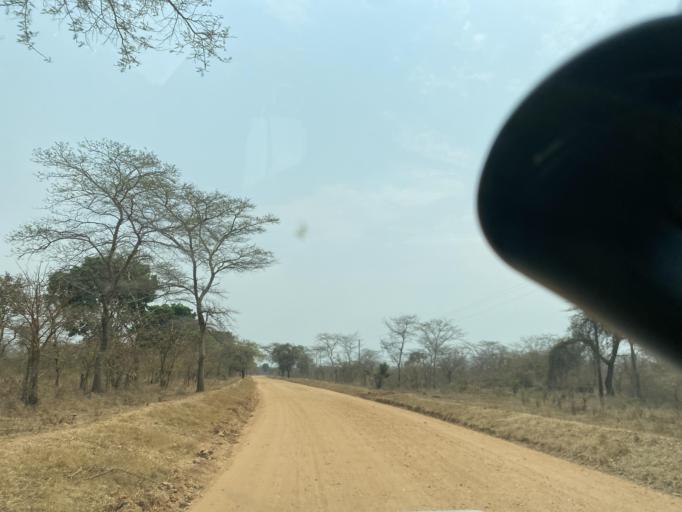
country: ZM
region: Lusaka
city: Kafue
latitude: -15.6113
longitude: 28.1083
